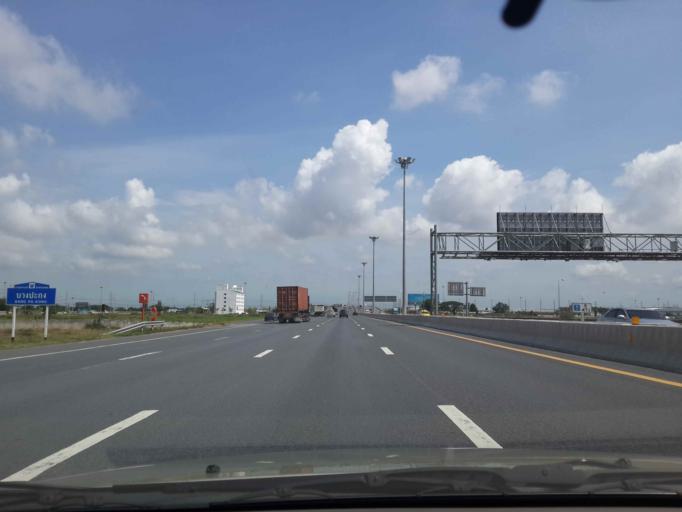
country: TH
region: Chachoengsao
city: Bang Pakong
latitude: 13.5531
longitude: 100.9973
